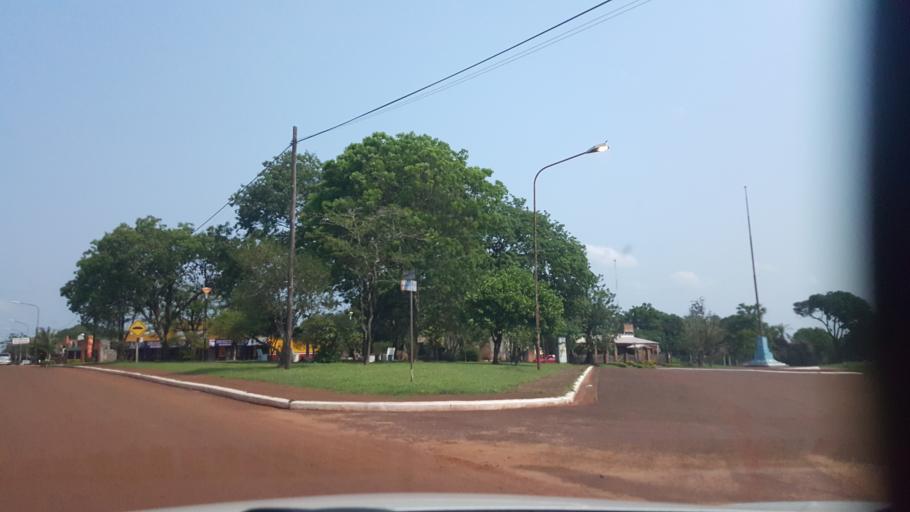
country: AR
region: Misiones
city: Santa Ana
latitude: -27.3689
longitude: -55.5821
